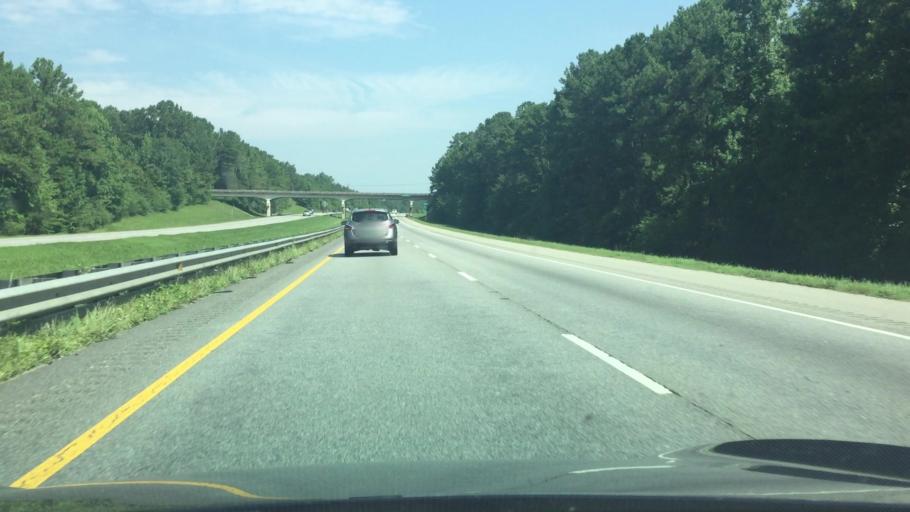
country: US
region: Alabama
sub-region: Shelby County
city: Calera
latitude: 33.0824
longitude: -86.7351
